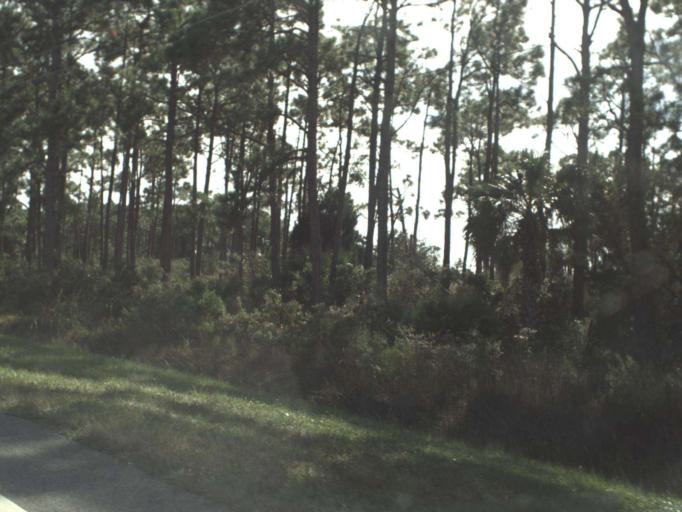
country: US
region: Florida
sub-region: Gulf County
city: Port Saint Joe
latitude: 29.7851
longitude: -85.3012
